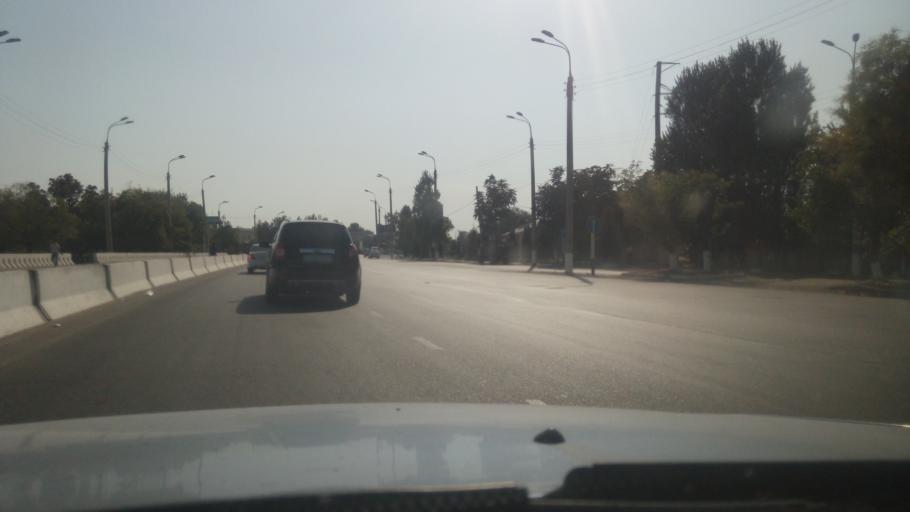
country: UZ
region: Toshkent
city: Urtaowul
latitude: 41.2369
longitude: 69.1661
